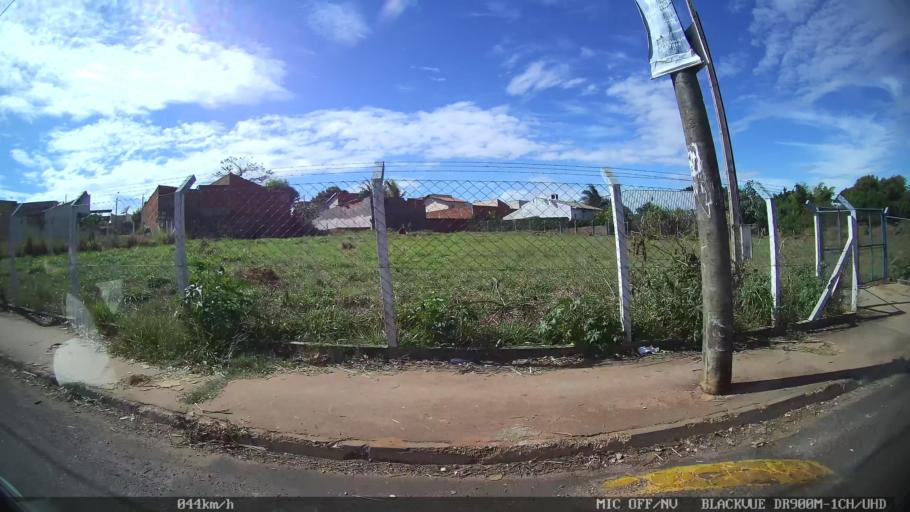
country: BR
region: Sao Paulo
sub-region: Bady Bassitt
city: Bady Bassitt
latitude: -20.8257
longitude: -49.4939
